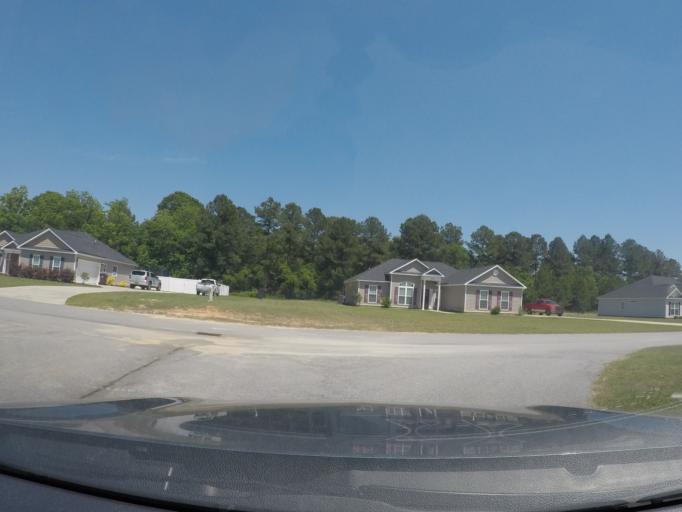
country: US
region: Georgia
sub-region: Bulloch County
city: Brooklet
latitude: 32.3514
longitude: -81.7543
